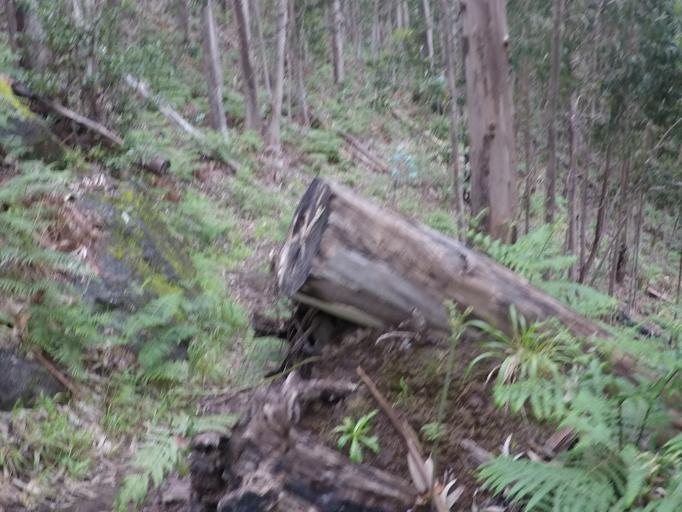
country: PT
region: Madeira
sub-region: Camara de Lobos
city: Curral das Freiras
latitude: 32.7471
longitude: -17.0158
